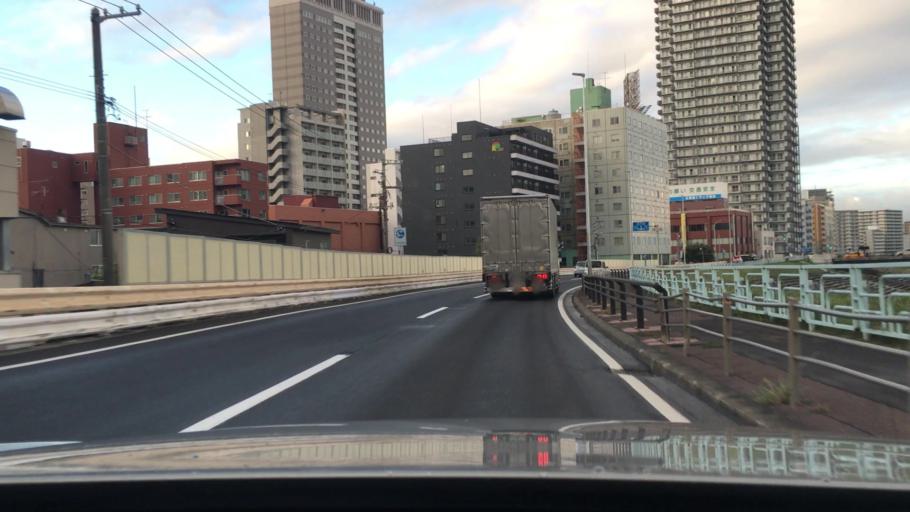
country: JP
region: Hokkaido
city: Sapporo
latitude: 43.0471
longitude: 141.3581
